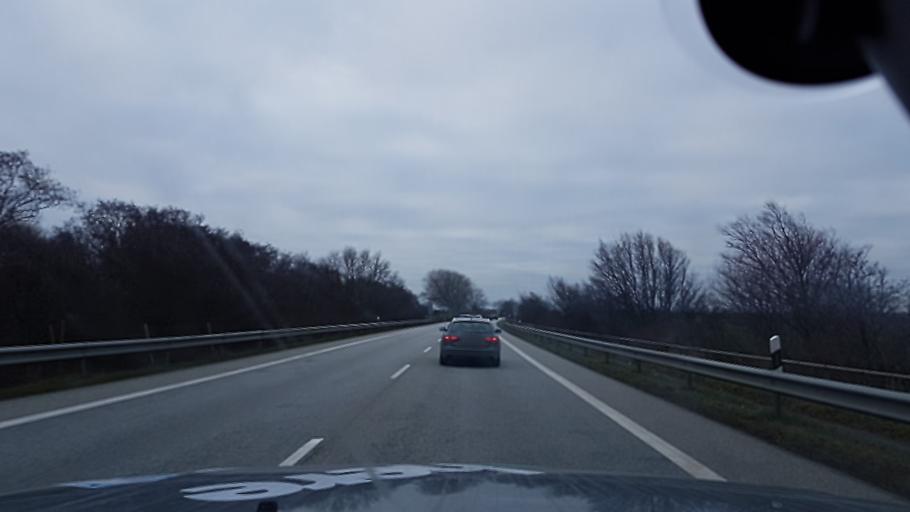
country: DE
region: Schleswig-Holstein
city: Grossenbrode
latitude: 54.3894
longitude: 11.1038
